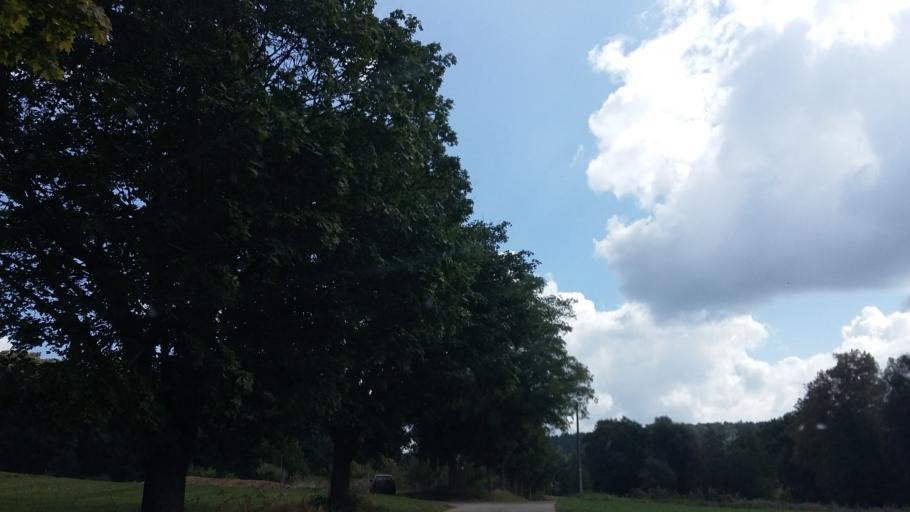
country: DE
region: Bavaria
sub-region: Swabia
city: Jettingen-Scheppach
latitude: 48.4033
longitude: 10.4581
